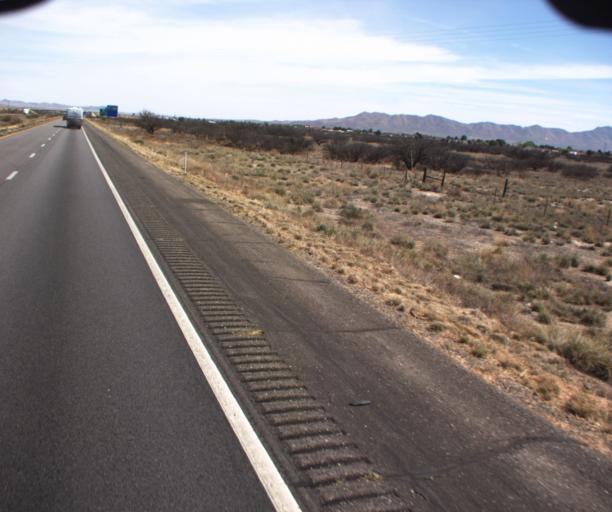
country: US
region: Arizona
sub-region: Cochise County
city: Willcox
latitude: 32.2468
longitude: -109.8589
